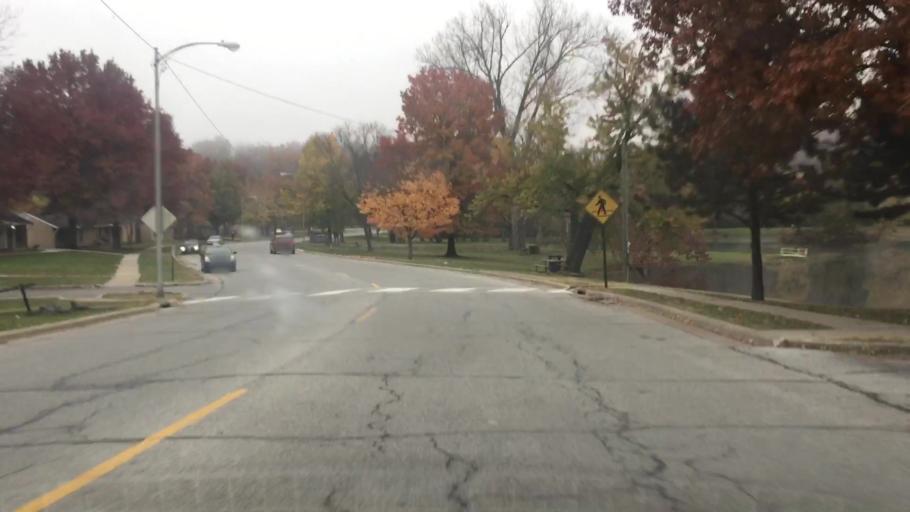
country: US
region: Missouri
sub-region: Callaway County
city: Fulton
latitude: 38.8460
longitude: -91.9543
